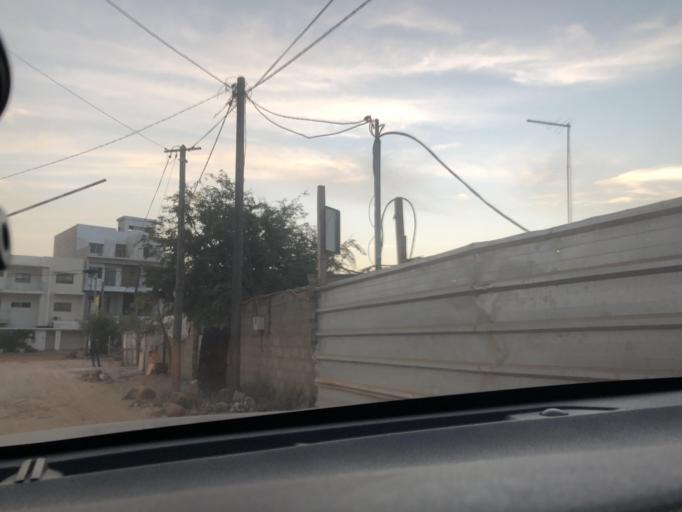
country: SN
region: Dakar
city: Mermoz Boabab
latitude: 14.7392
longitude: -17.5157
